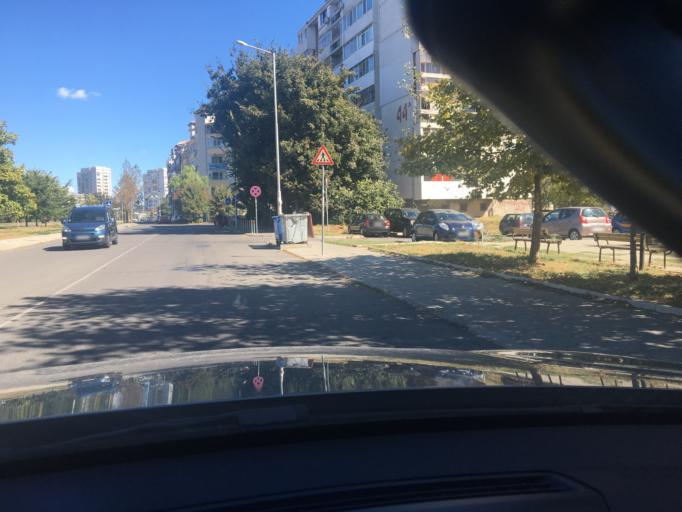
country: BG
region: Burgas
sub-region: Obshtina Burgas
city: Burgas
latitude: 42.5232
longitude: 27.4622
